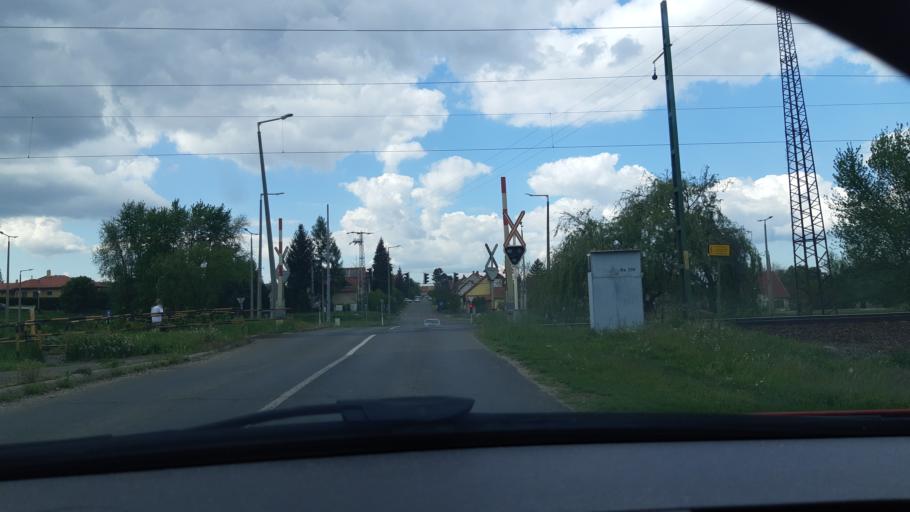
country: HU
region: Somogy
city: Kaposvar
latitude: 46.3651
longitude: 17.7597
